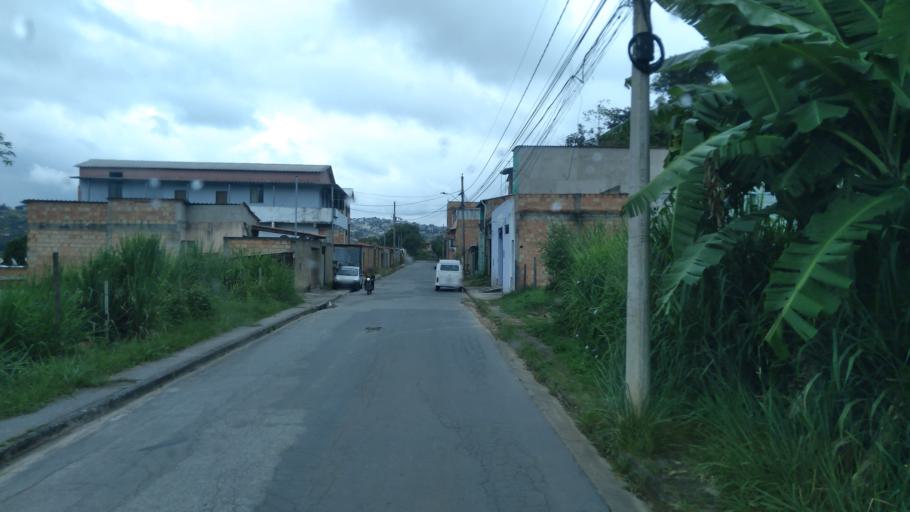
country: BR
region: Minas Gerais
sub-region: Santa Luzia
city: Santa Luzia
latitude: -19.8374
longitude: -43.8701
